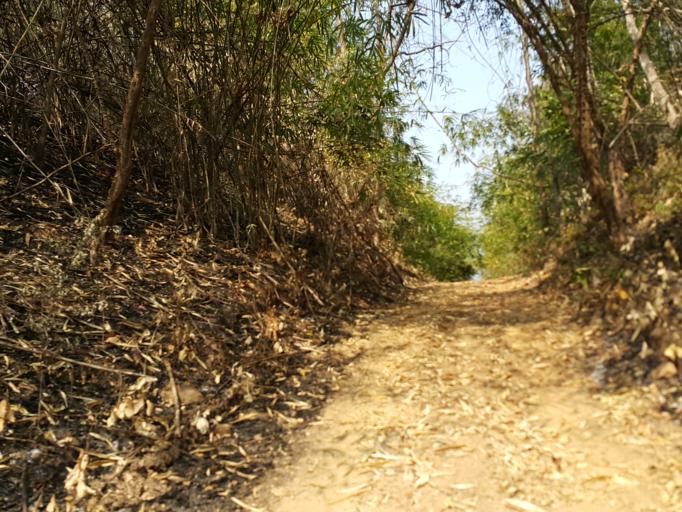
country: TH
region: Sukhothai
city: Thung Saliam
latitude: 17.3228
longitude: 99.4998
